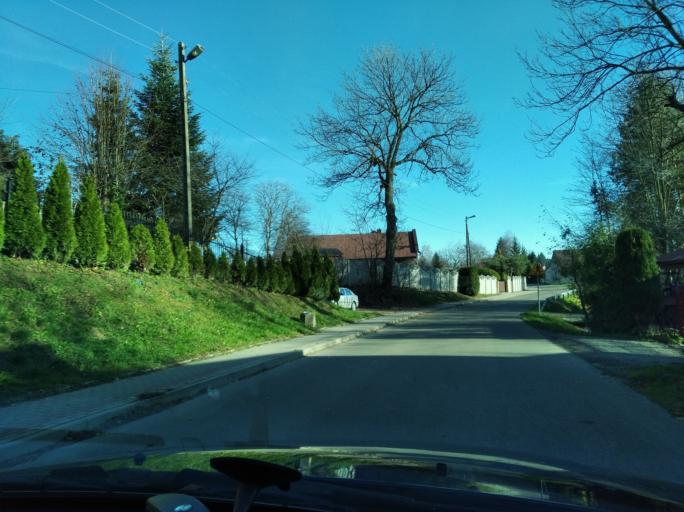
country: PL
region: Subcarpathian Voivodeship
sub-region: Powiat rzeszowski
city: Lutoryz
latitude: 49.9672
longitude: 21.9073
